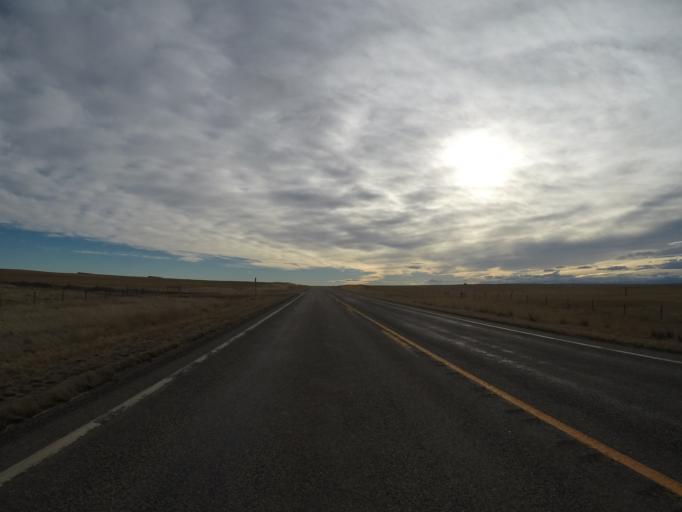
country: US
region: Montana
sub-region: Yellowstone County
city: Laurel
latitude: 45.8426
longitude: -108.8812
